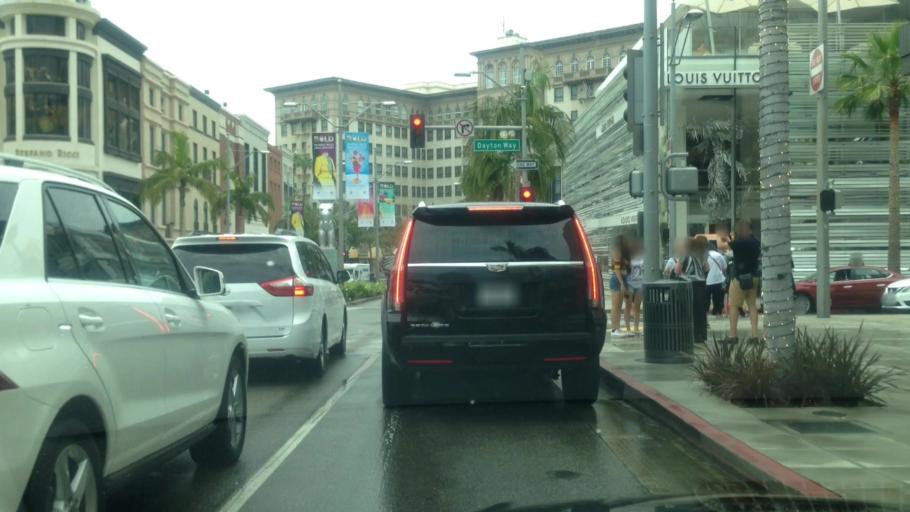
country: US
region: California
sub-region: Los Angeles County
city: Beverly Hills
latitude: 34.0680
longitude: -118.4019
